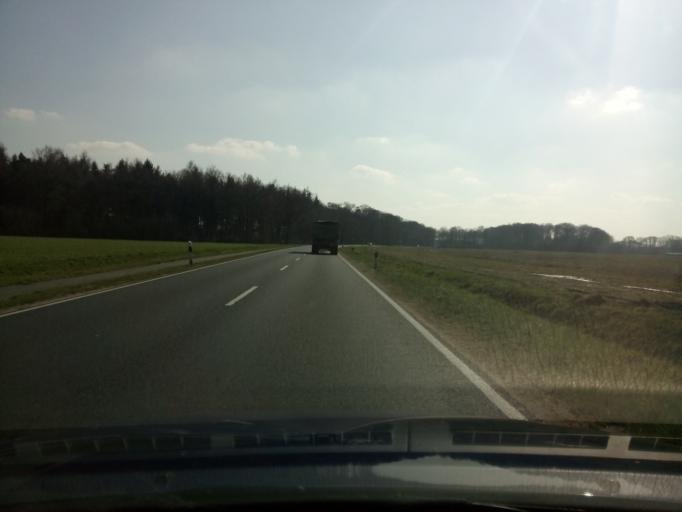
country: DE
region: Lower Saxony
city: Isterberg
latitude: 52.3372
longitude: 7.0710
